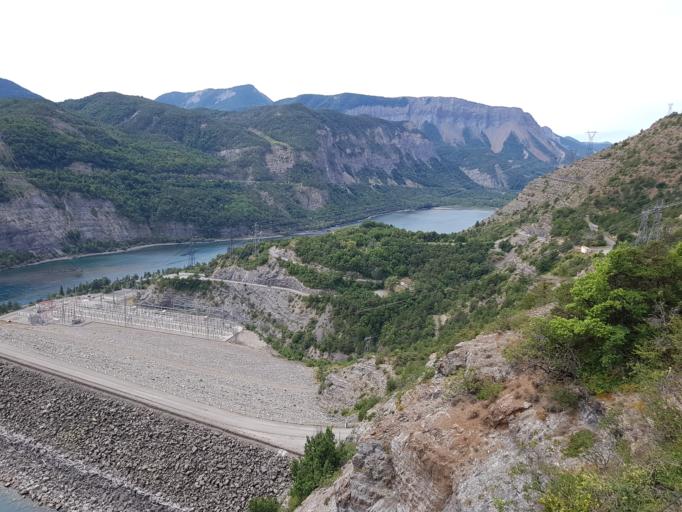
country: FR
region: Provence-Alpes-Cote d'Azur
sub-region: Departement des Hautes-Alpes
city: Chorges
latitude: 44.4748
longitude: 6.2696
